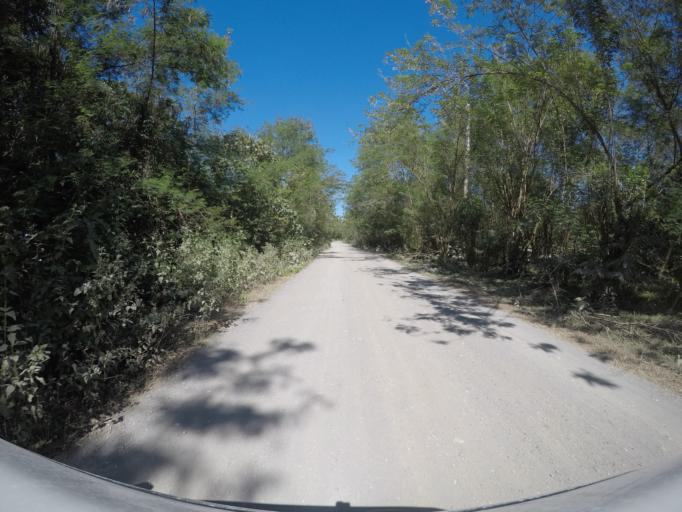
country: TL
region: Viqueque
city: Viqueque
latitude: -8.9738
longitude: 126.0670
